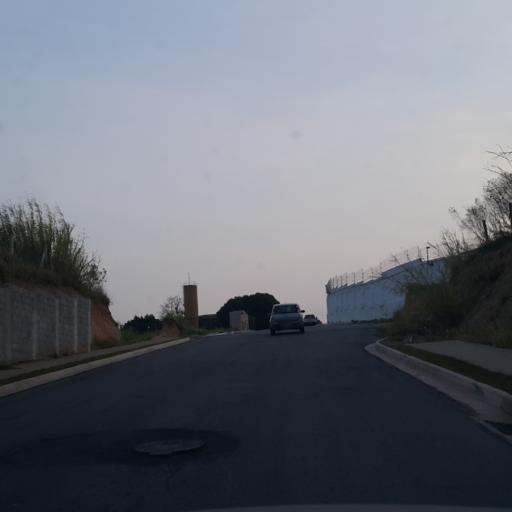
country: BR
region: Sao Paulo
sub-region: Vinhedo
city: Vinhedo
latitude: -23.0462
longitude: -46.9771
